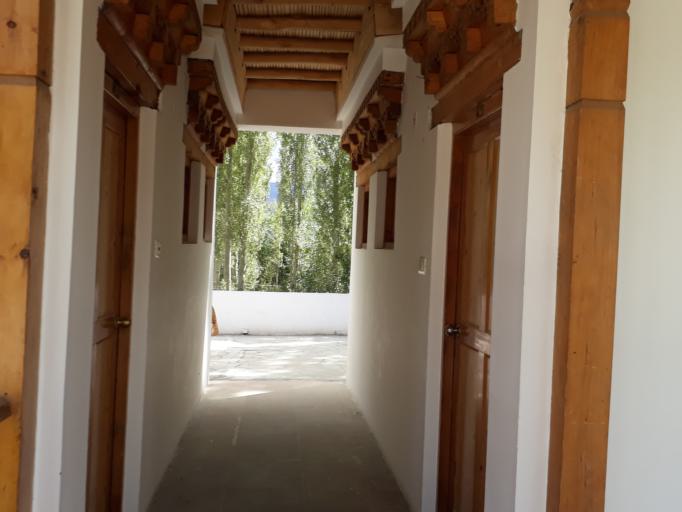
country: IN
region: Kashmir
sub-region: Ladakh
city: Leh
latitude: 34.1520
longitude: 77.5717
